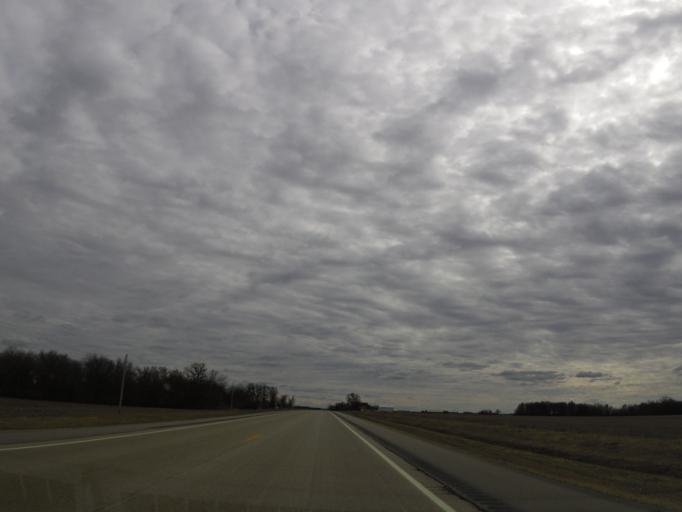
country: US
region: Minnesota
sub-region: Fillmore County
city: Spring Valley
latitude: 43.5201
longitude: -92.3695
